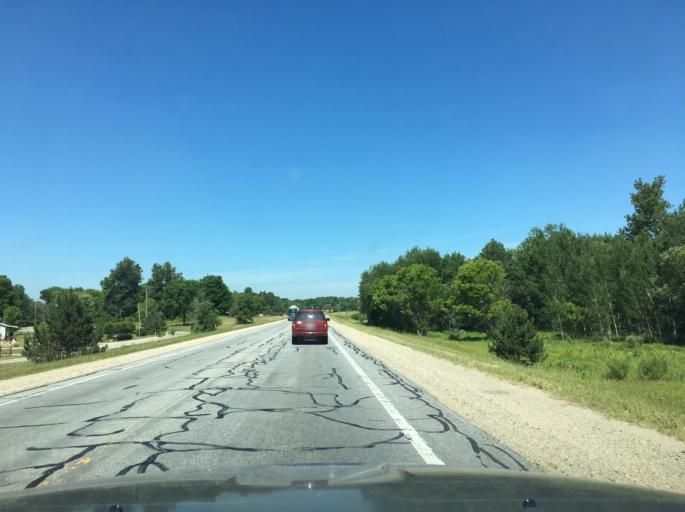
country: US
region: Michigan
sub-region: Osceola County
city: Reed City
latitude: 43.8803
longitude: -85.5040
